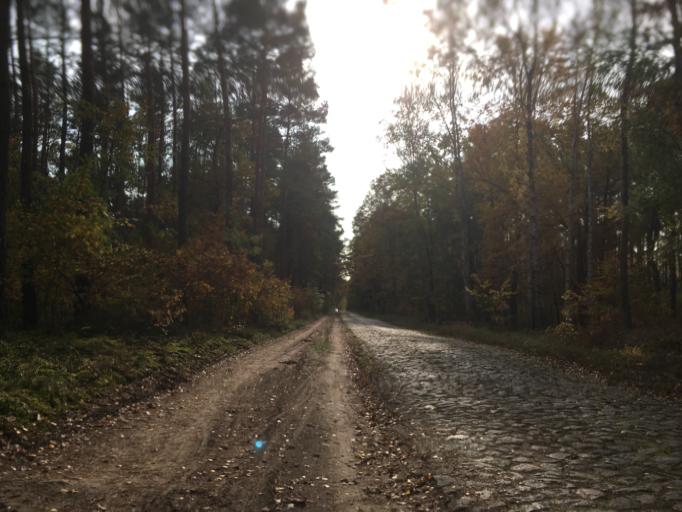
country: DE
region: Brandenburg
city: Liebenwalde
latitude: 52.9656
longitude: 13.4853
